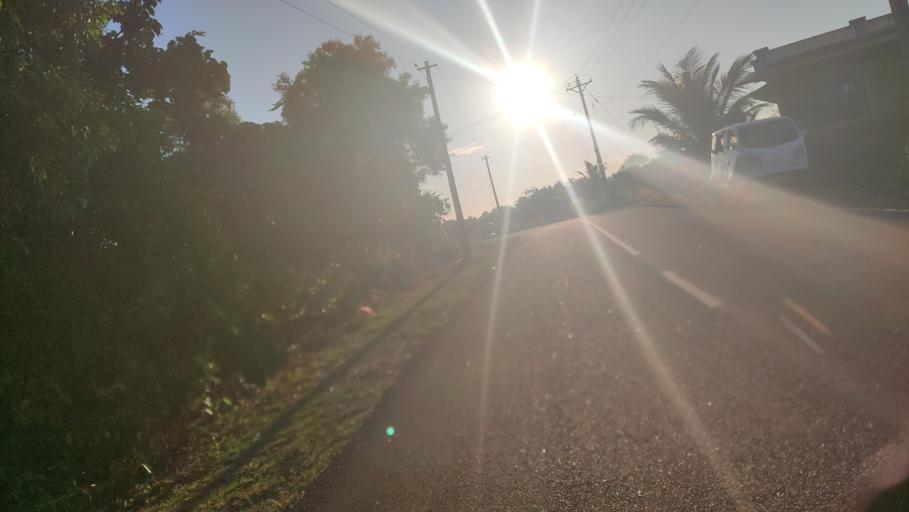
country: IN
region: Kerala
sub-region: Kasaragod District
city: Kasaragod
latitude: 12.4560
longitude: 75.0972
